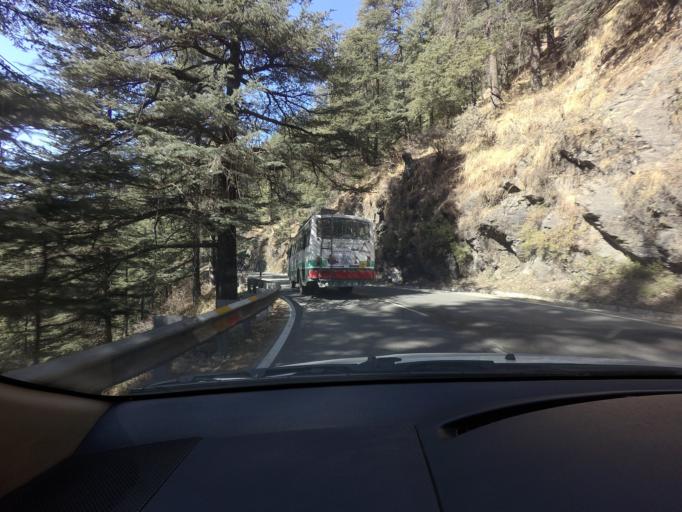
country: IN
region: Himachal Pradesh
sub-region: Shimla
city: Shimla
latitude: 31.1193
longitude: 77.2366
